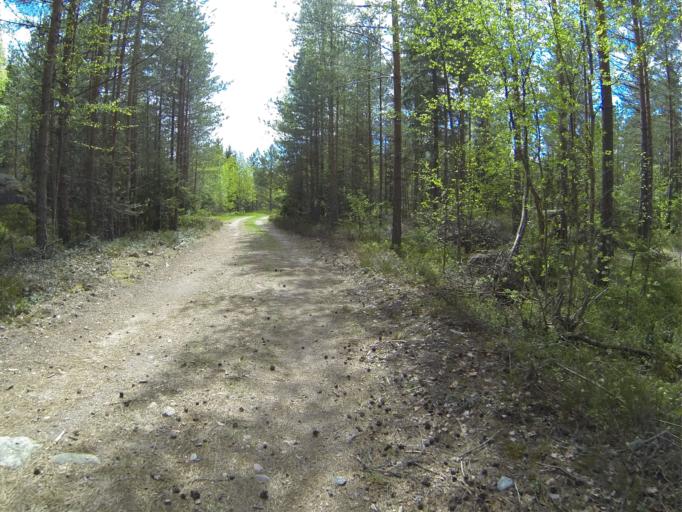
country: FI
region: Varsinais-Suomi
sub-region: Salo
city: Halikko
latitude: 60.3069
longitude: 23.0758
